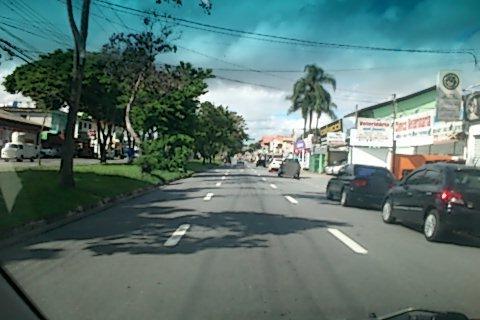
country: BR
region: Sao Paulo
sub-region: Sao Jose Dos Campos
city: Sao Jose dos Campos
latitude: -23.2369
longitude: -45.8850
